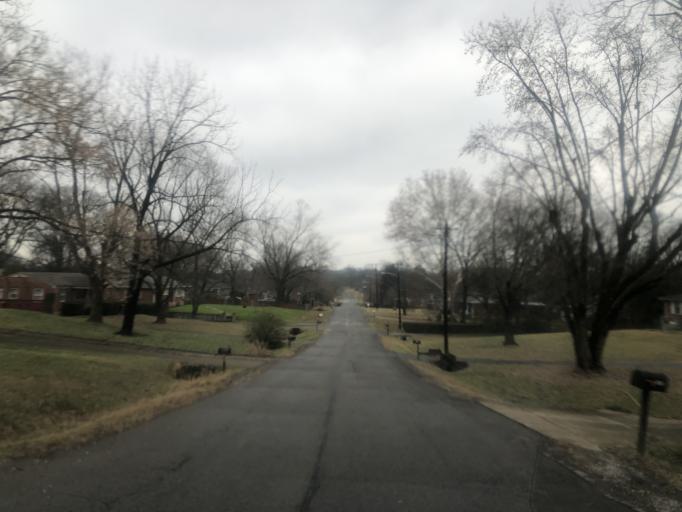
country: US
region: Tennessee
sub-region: Davidson County
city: Lakewood
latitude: 36.1514
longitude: -86.6624
